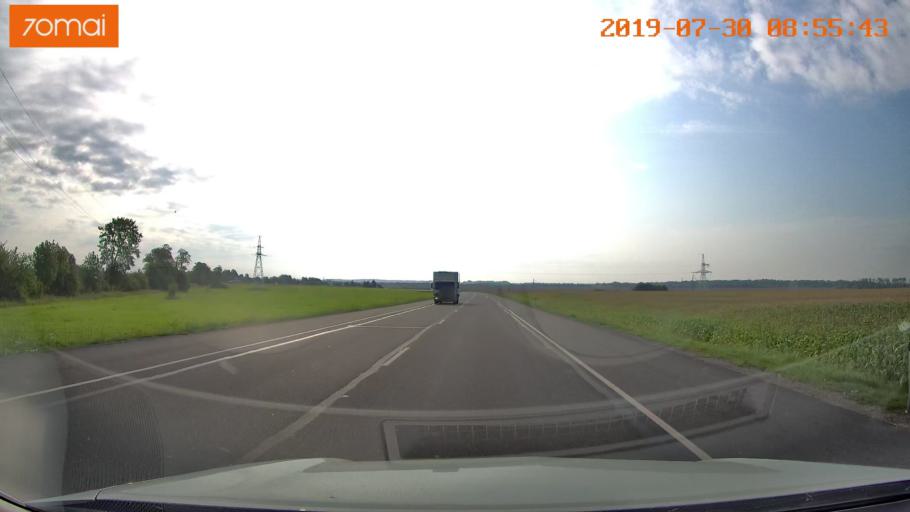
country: RU
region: Kaliningrad
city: Gusev
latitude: 54.6000
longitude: 22.0590
